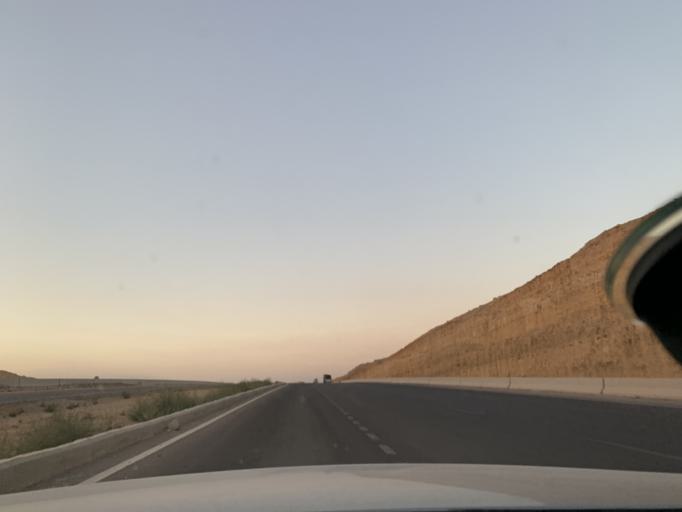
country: EG
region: Muhafazat al Qahirah
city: Halwan
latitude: 29.9510
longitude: 31.5389
